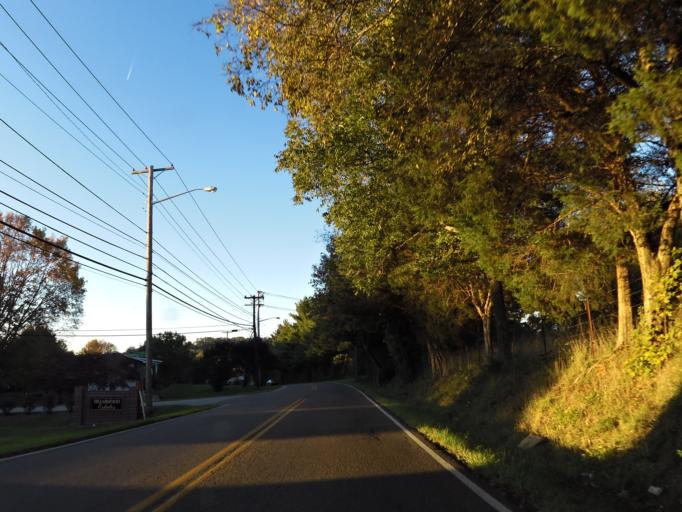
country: US
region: Tennessee
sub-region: Knox County
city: Knoxville
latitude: 36.0226
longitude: -83.9891
